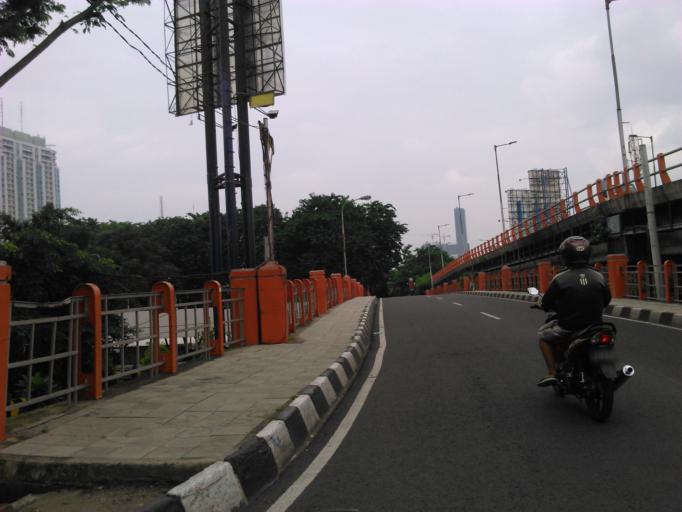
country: ID
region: East Java
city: Pacarkeling
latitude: -7.2644
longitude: 112.7528
